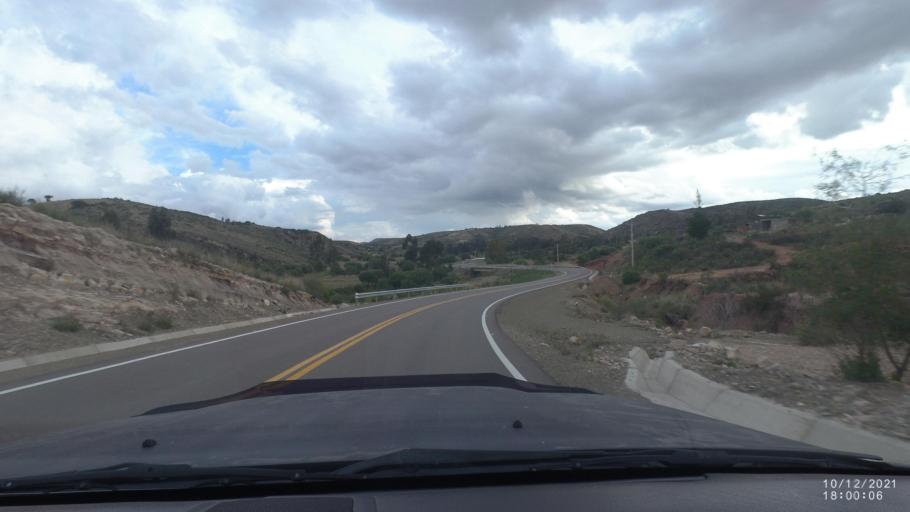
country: BO
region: Cochabamba
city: Cliza
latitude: -17.7389
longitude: -65.9223
